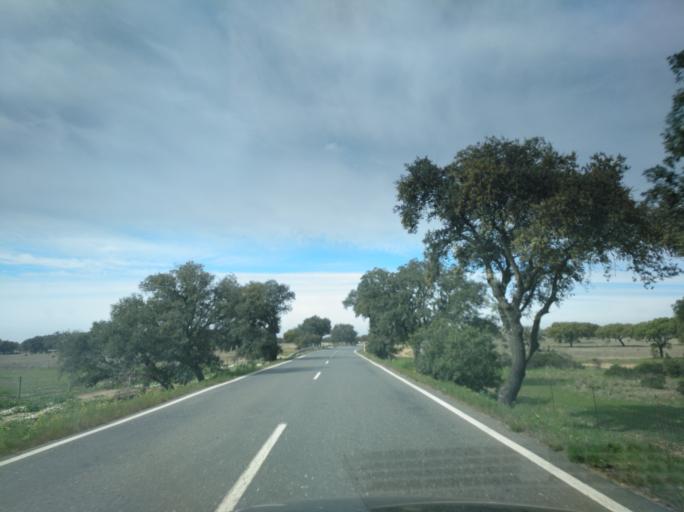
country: PT
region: Beja
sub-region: Mertola
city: Mertola
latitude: 37.7524
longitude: -7.8058
